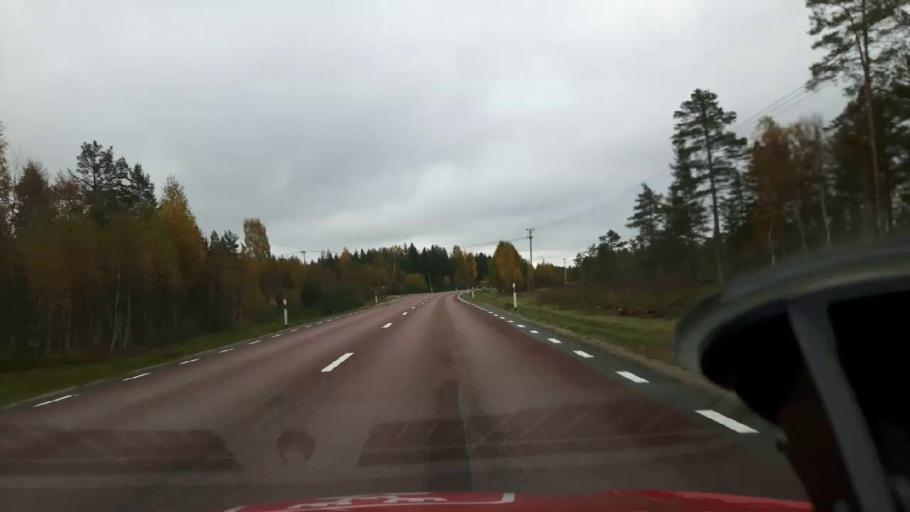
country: SE
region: Jaemtland
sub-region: Harjedalens Kommun
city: Sveg
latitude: 62.2622
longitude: 14.8137
